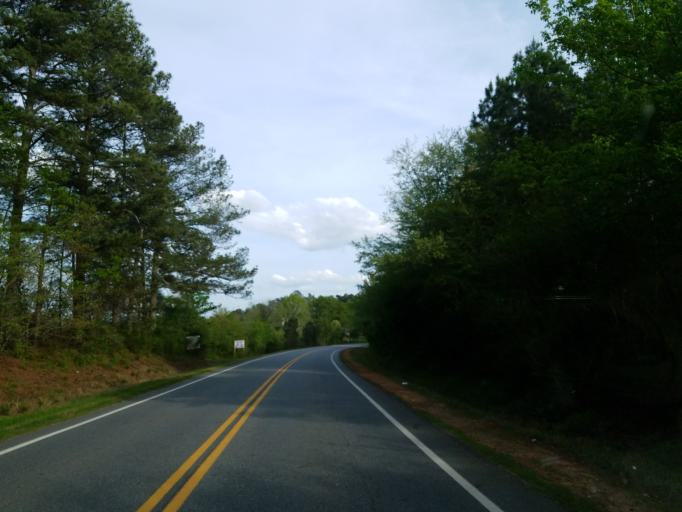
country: US
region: Georgia
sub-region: Pickens County
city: Nelson
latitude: 34.3537
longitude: -84.2688
